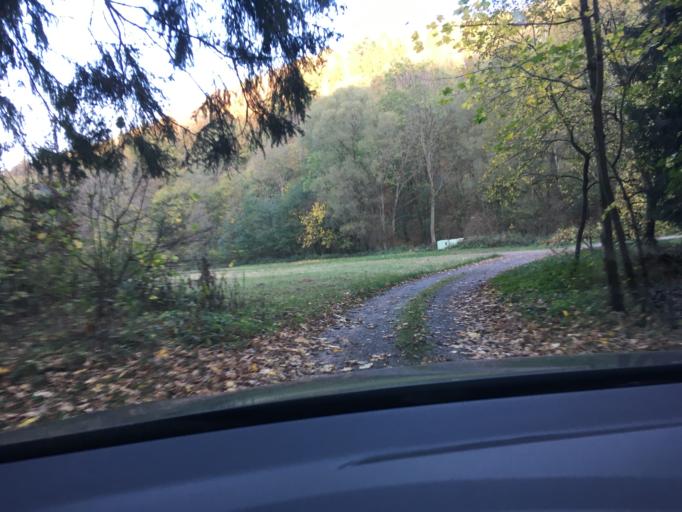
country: DE
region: Saxony
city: Barenstein
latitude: 50.8300
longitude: 13.8281
